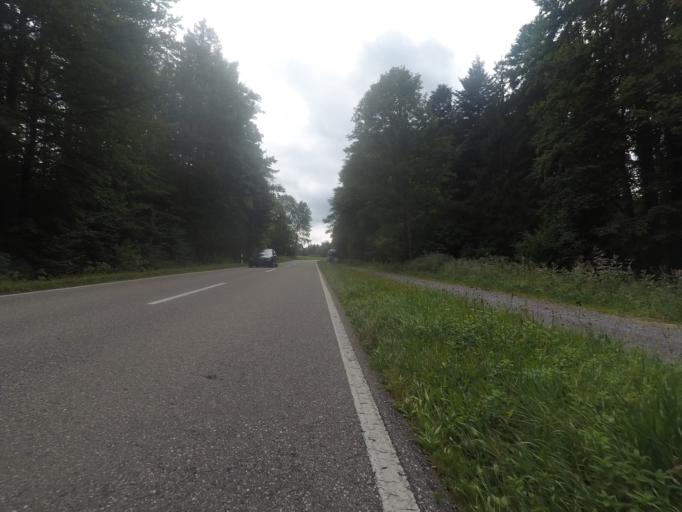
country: DE
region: Baden-Wuerttemberg
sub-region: Karlsruhe Region
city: Dobel
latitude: 48.8058
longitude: 8.4883
